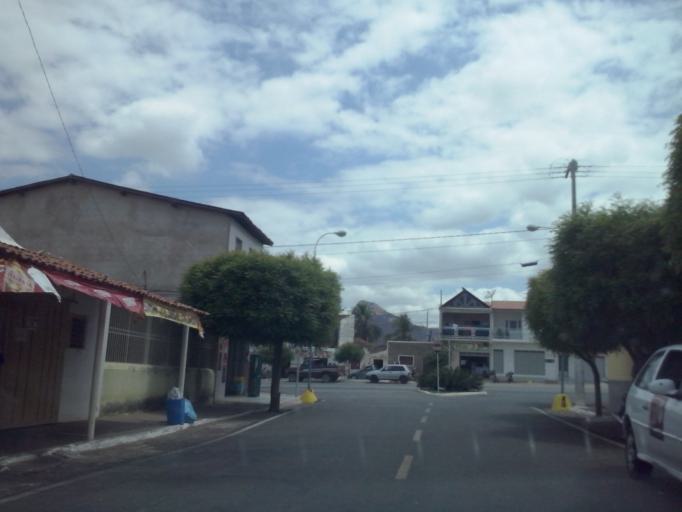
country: BR
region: Paraiba
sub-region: Patos
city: Patos
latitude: -6.9046
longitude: -37.5196
